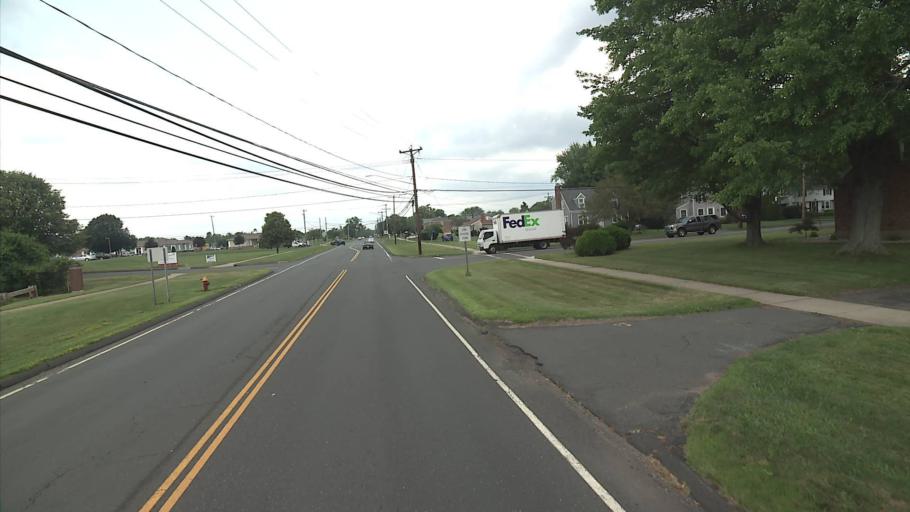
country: US
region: Connecticut
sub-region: Hartford County
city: Newington
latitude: 41.7034
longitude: -72.7350
